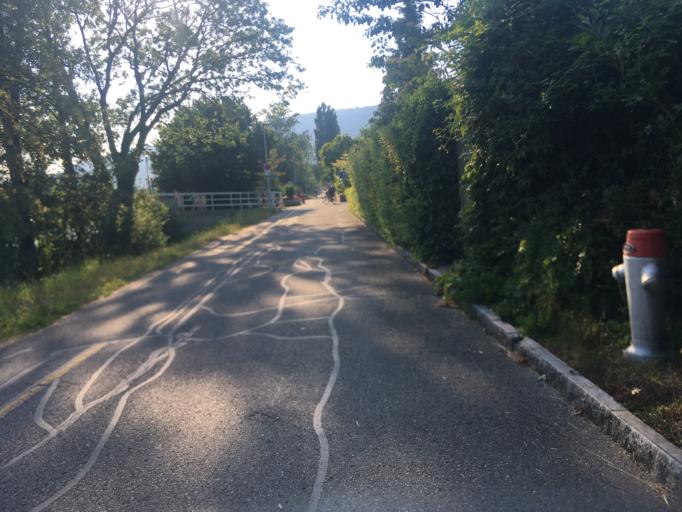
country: CH
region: Bern
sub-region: Biel/Bienne District
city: Bellmund
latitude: 47.1201
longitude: 7.2532
